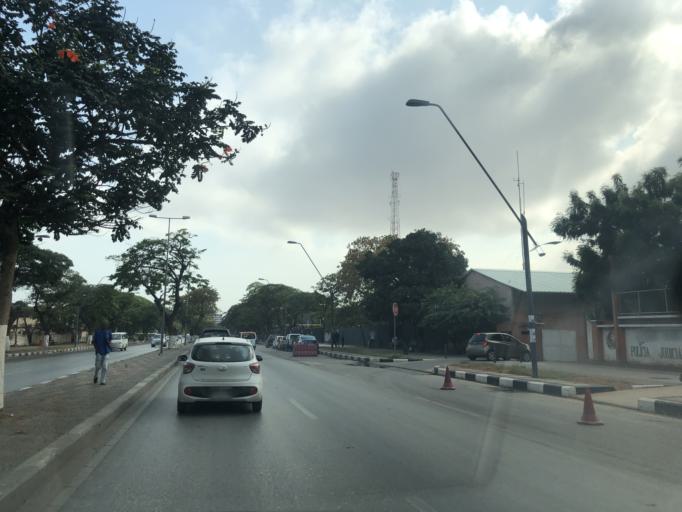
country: AO
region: Luanda
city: Luanda
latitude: -8.8366
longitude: 13.2374
